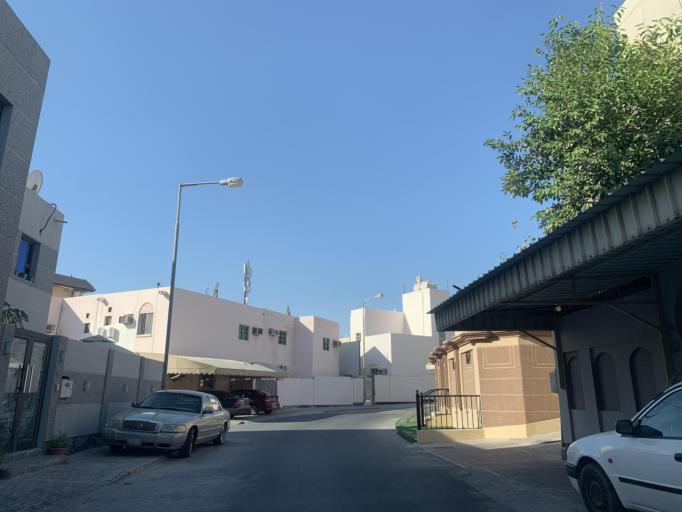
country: BH
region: Central Governorate
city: Madinat Hamad
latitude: 26.1037
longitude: 50.5083
